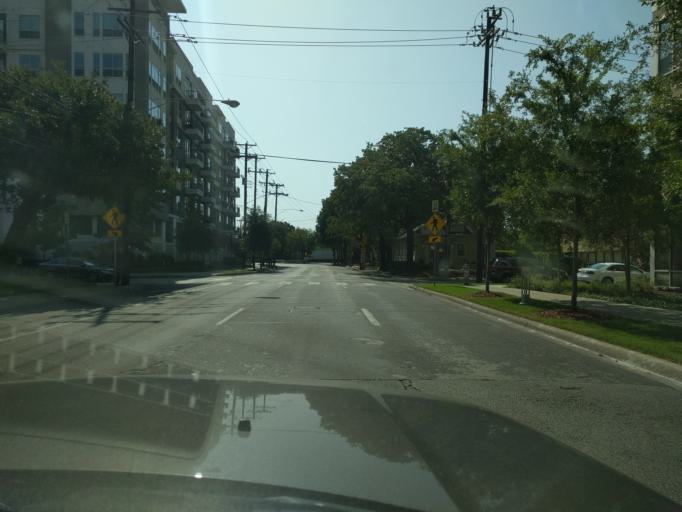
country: US
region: Texas
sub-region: Dallas County
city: Dallas
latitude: 32.8049
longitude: -96.7973
